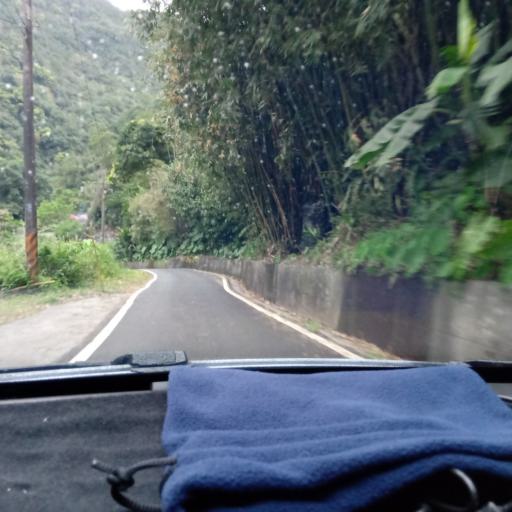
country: TW
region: Taiwan
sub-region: Yilan
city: Yilan
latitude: 24.8075
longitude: 121.7011
